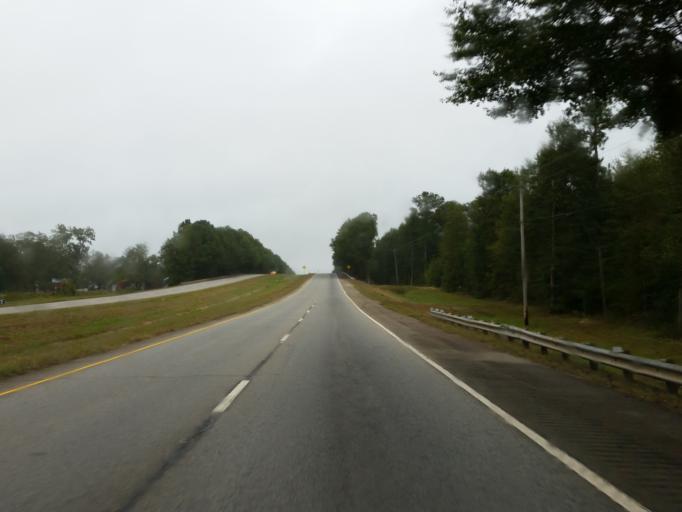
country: US
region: Georgia
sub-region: Lamar County
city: Barnesville
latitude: 33.1108
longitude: -84.2016
